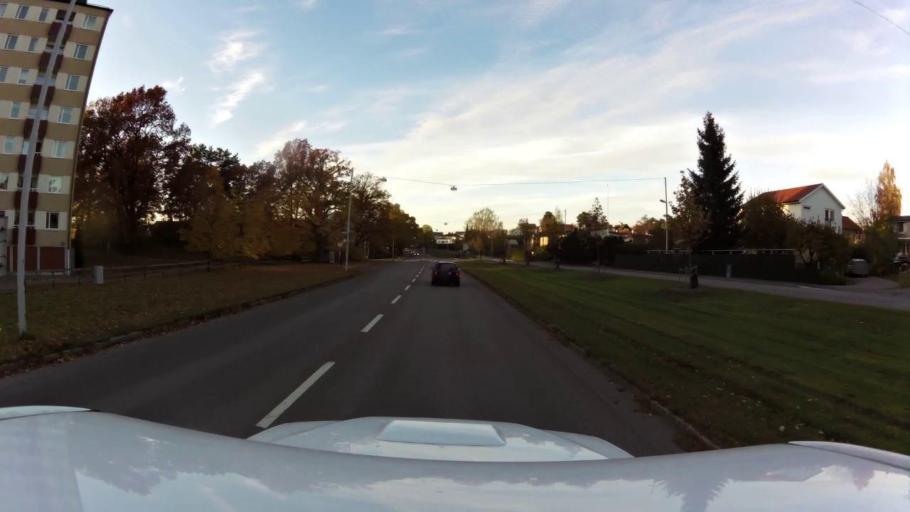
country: SE
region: OEstergoetland
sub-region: Linkopings Kommun
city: Linkoping
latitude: 58.3948
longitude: 15.6437
